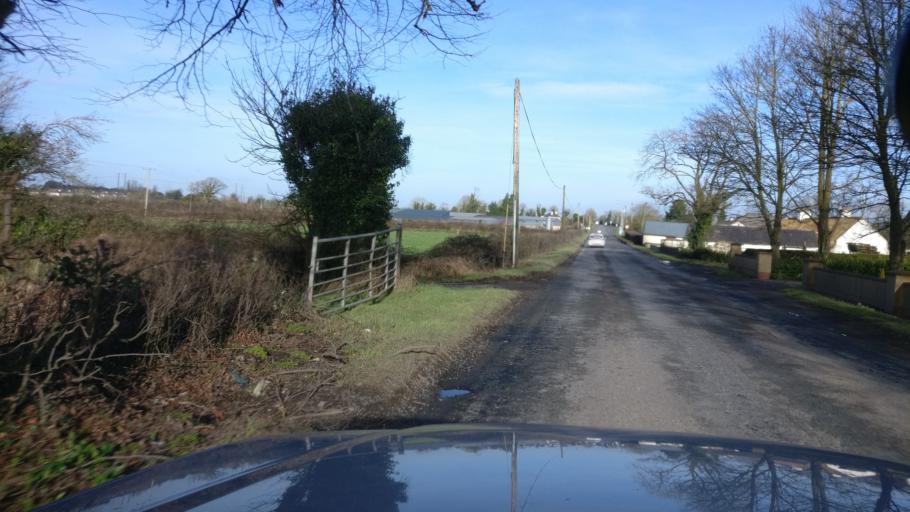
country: IE
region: Leinster
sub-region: Laois
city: Portlaoise
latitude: 53.0230
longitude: -7.2706
